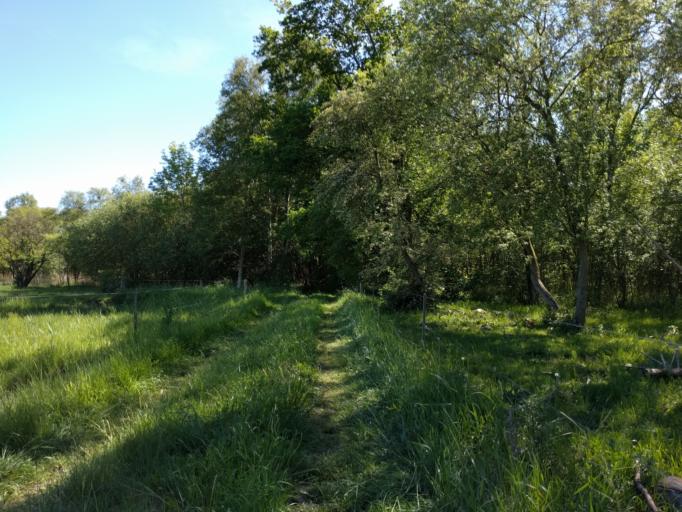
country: DK
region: South Denmark
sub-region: Kerteminde Kommune
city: Langeskov
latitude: 55.3845
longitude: 10.5904
